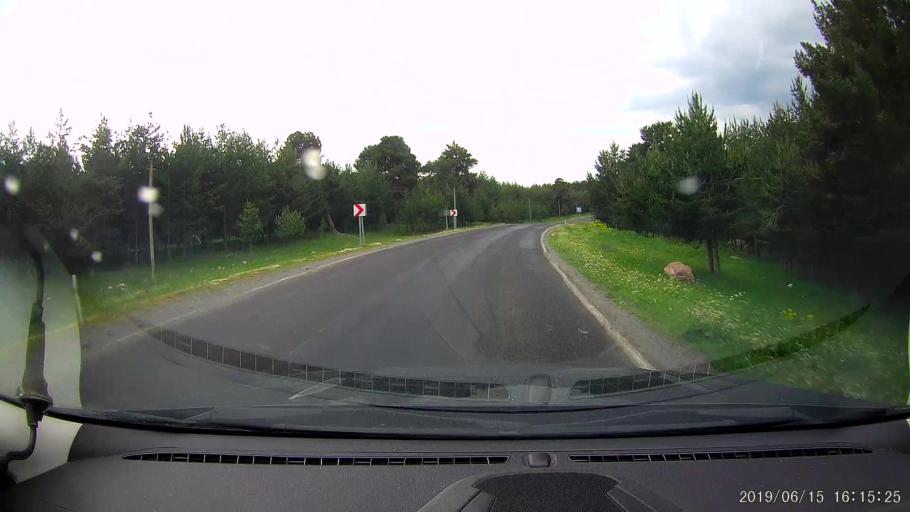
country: TR
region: Ardahan
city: Hanak
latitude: 41.2687
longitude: 42.8561
